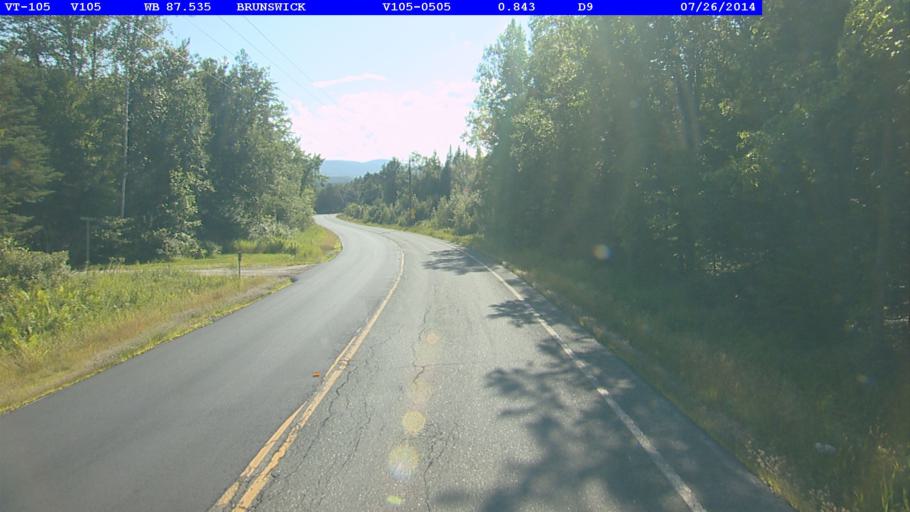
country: US
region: New Hampshire
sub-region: Coos County
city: Stratford
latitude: 44.7661
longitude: -71.7063
